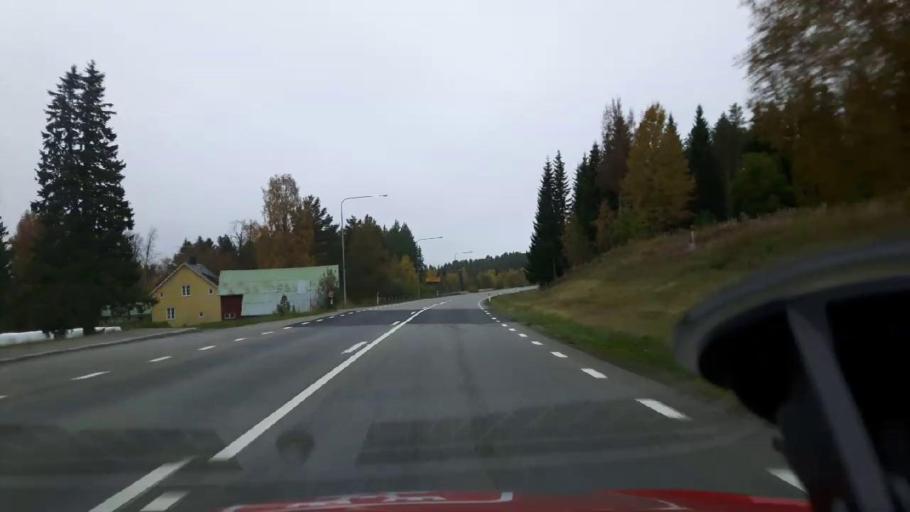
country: SE
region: Jaemtland
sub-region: Bergs Kommun
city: Hoverberg
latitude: 62.6607
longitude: 14.3808
